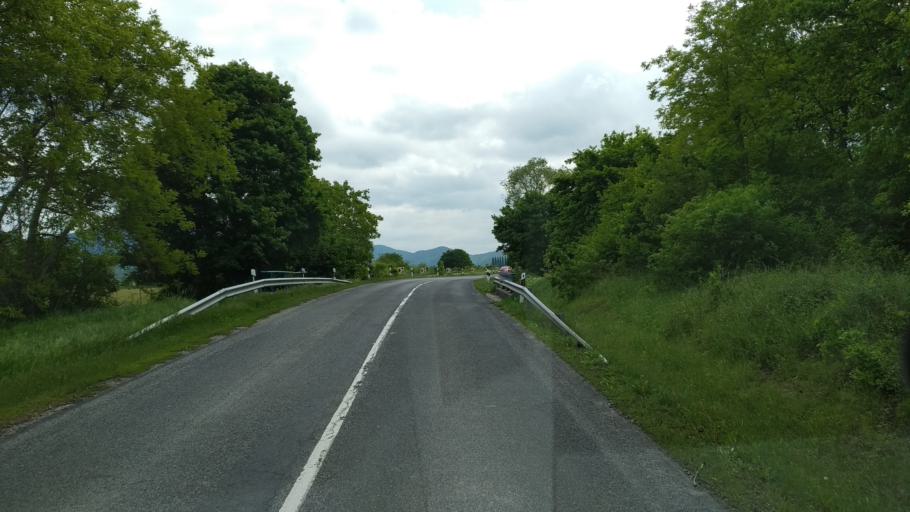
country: HU
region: Komarom-Esztergom
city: Pilismarot
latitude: 47.7963
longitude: 18.8630
